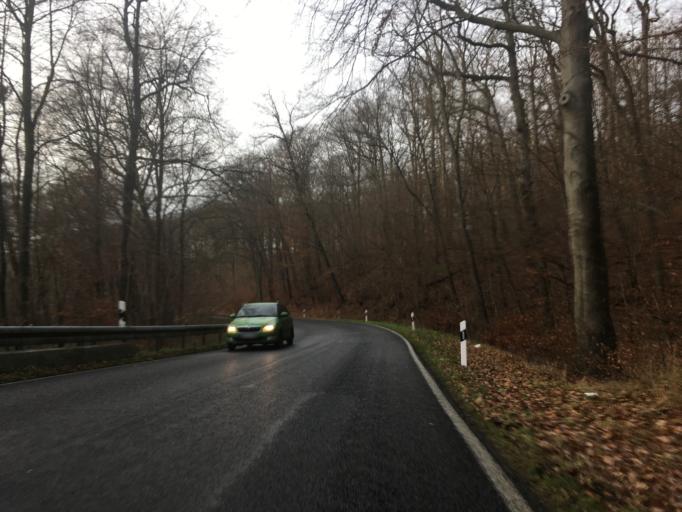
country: DE
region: Brandenburg
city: Eberswalde
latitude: 52.8536
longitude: 13.8538
